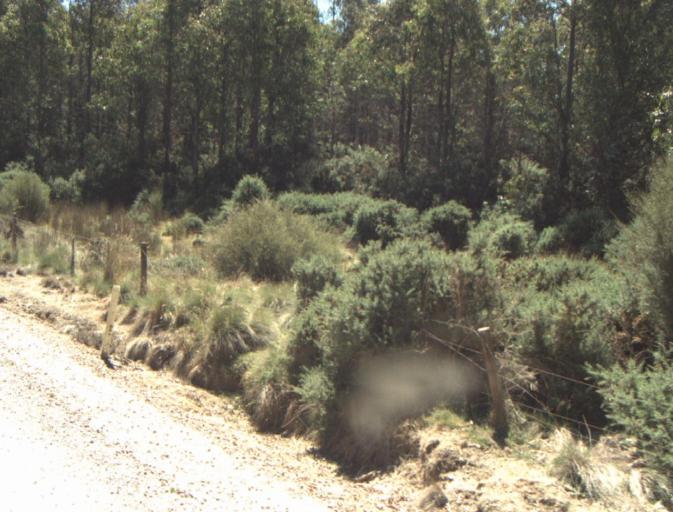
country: AU
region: Tasmania
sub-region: Dorset
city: Scottsdale
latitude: -41.3241
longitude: 147.4737
